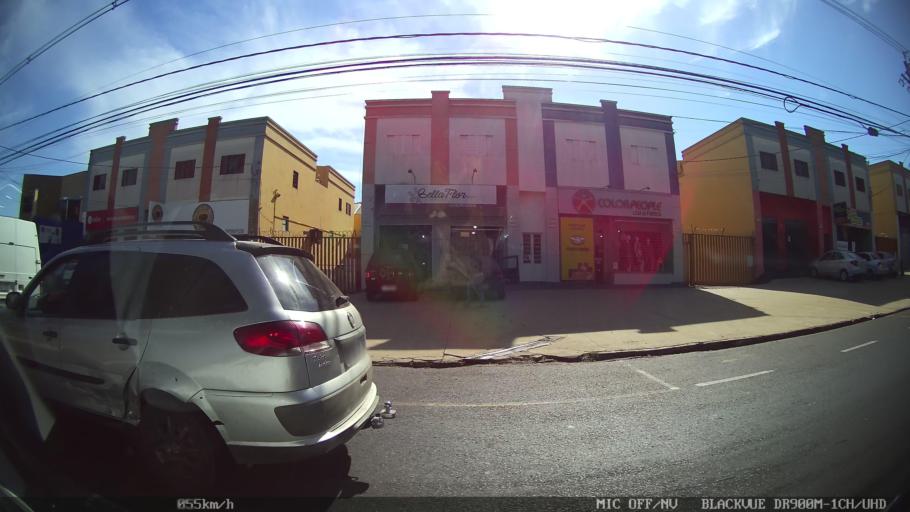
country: BR
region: Sao Paulo
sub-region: Franca
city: Franca
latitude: -20.5108
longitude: -47.4021
